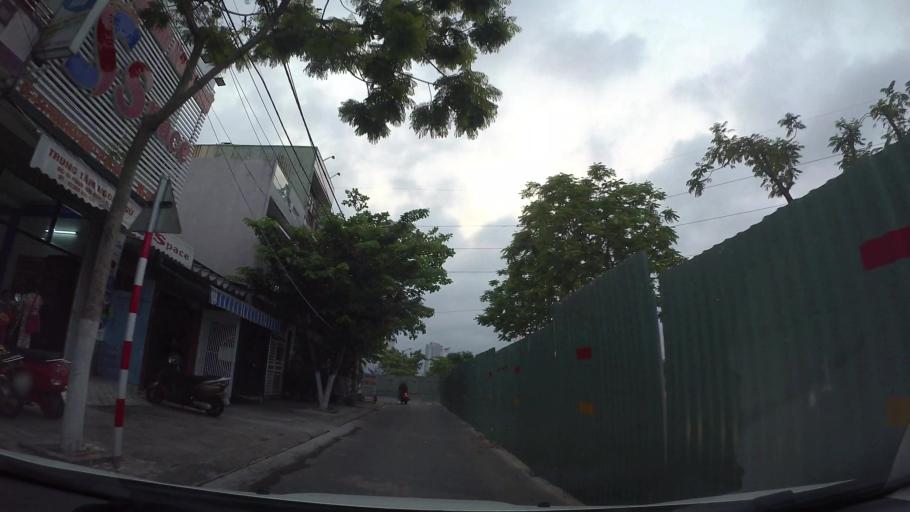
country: VN
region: Da Nang
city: Son Tra
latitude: 16.0504
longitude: 108.2358
